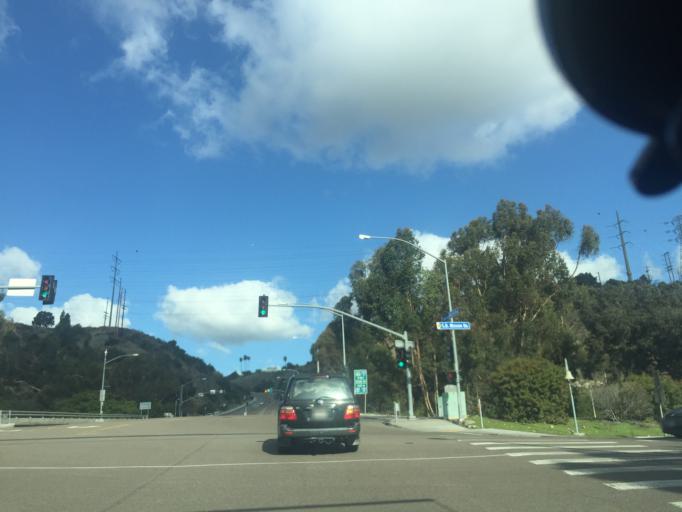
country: US
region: California
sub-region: San Diego County
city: San Diego
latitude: 32.7860
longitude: -117.1200
